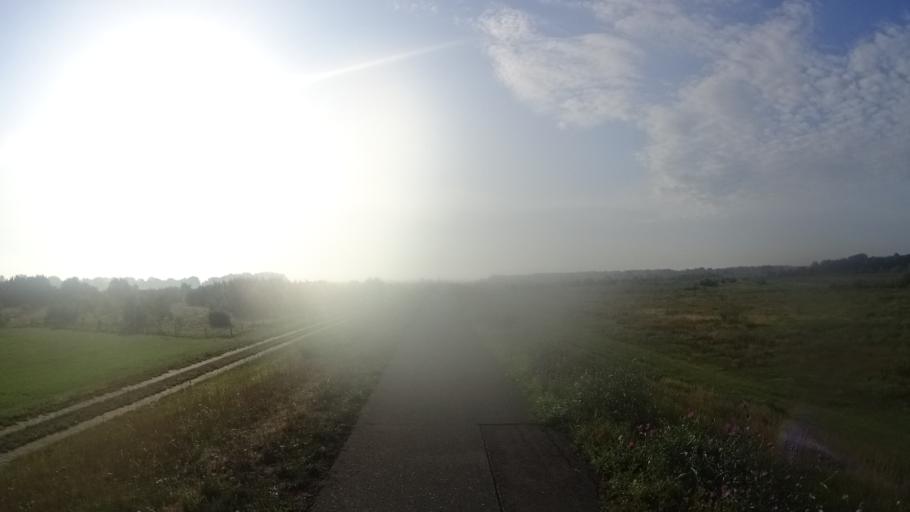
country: DE
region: Brandenburg
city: Lenzen
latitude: 53.0599
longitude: 11.5205
